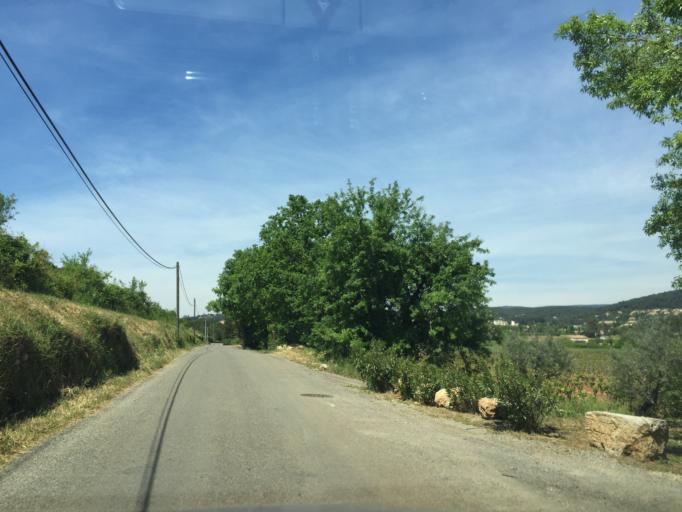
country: FR
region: Provence-Alpes-Cote d'Azur
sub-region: Departement du Var
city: Lorgues
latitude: 43.4796
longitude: 6.3678
